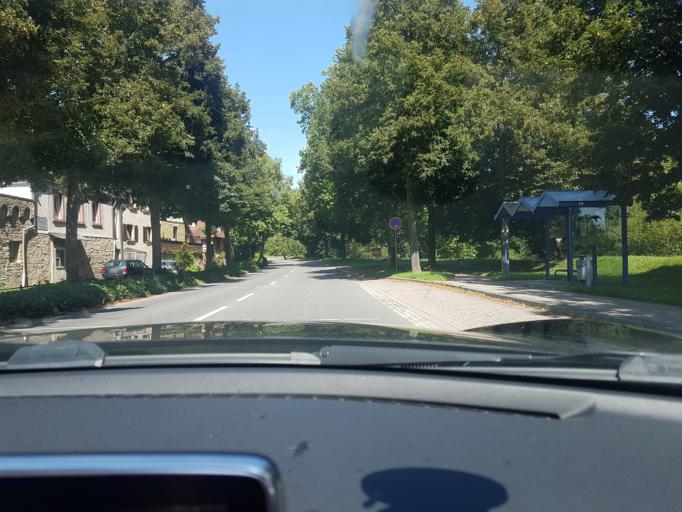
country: DE
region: Baden-Wuerttemberg
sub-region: Regierungsbezirk Stuttgart
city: Mockmuhl
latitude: 49.3229
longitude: 9.3627
